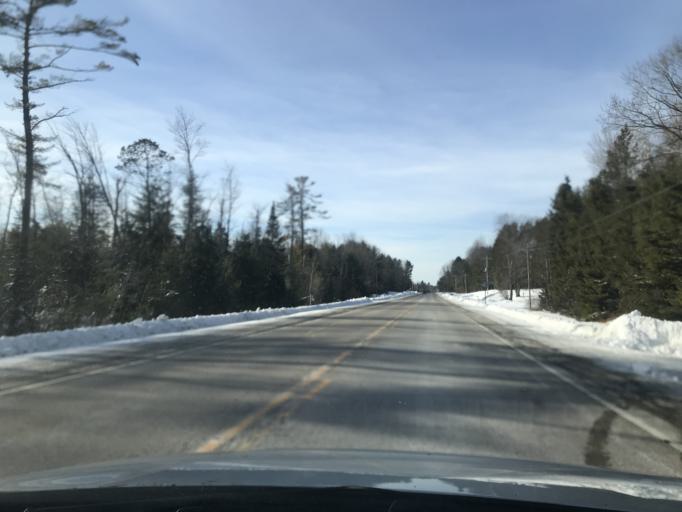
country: US
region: Wisconsin
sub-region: Oconto County
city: Gillett
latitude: 45.1288
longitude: -88.4148
